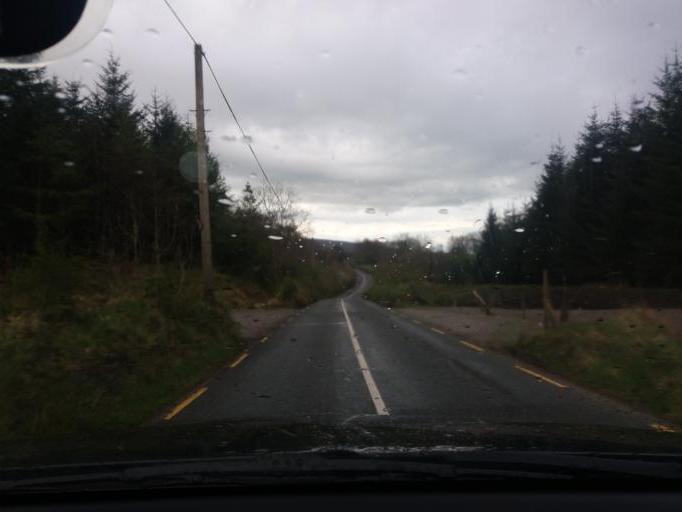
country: IE
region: Ulster
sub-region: An Cabhan
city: Ballyconnell
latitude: 54.1562
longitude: -7.7297
